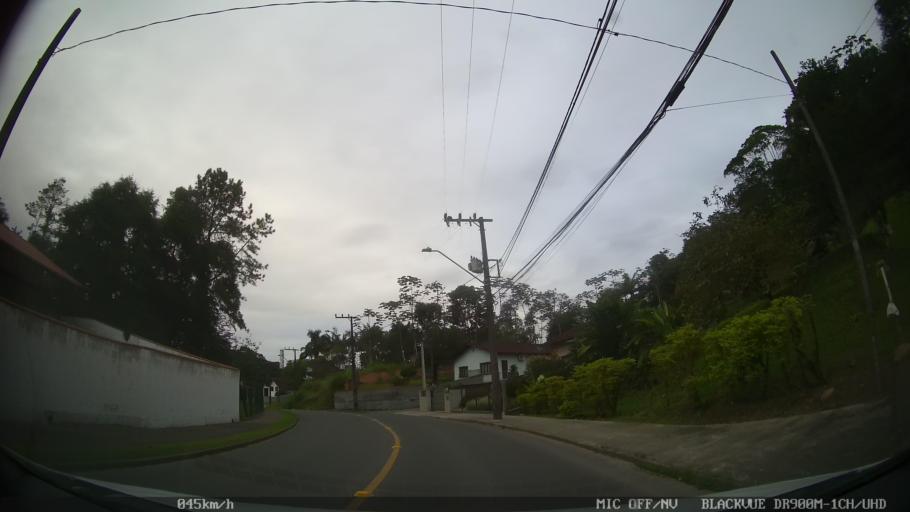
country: BR
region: Santa Catarina
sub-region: Joinville
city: Joinville
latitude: -26.2821
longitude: -48.8655
